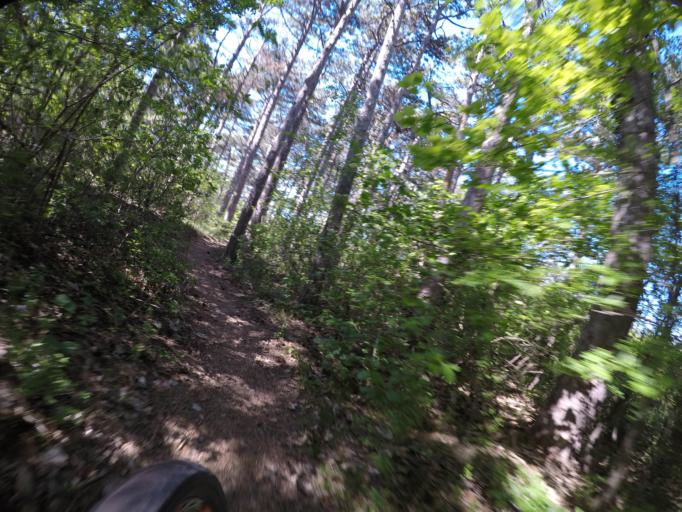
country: AT
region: Lower Austria
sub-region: Politischer Bezirk Modling
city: Modling
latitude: 48.0689
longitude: 16.2812
